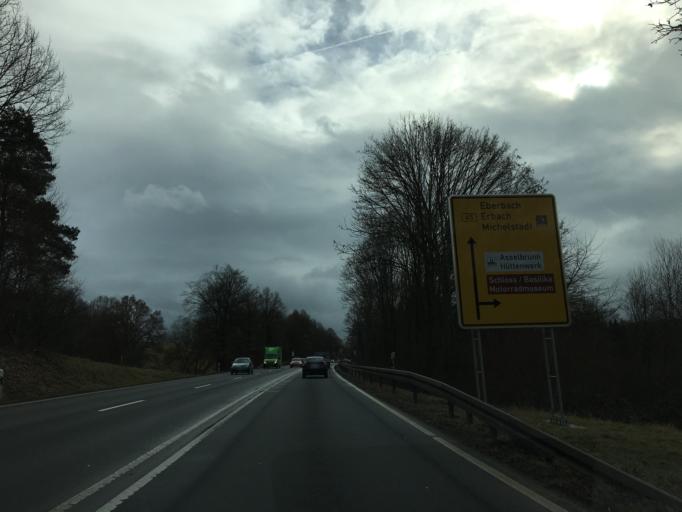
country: DE
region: Hesse
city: Michelstadt
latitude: 49.6939
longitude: 9.0069
